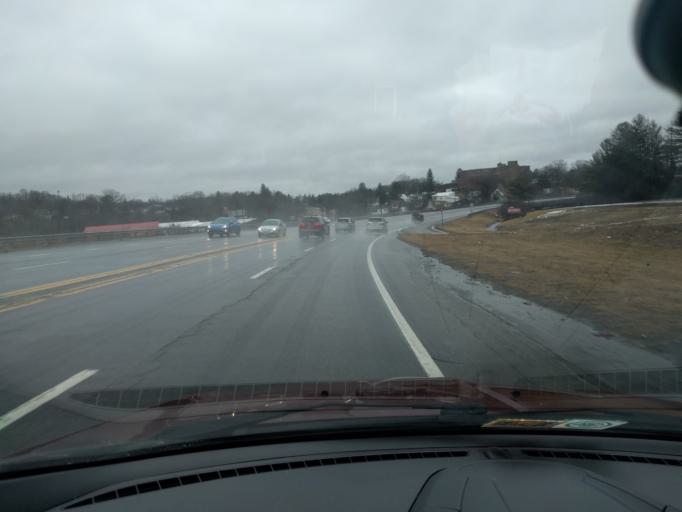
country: US
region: West Virginia
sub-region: Raleigh County
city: Mabscott
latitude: 37.7649
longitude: -81.2057
